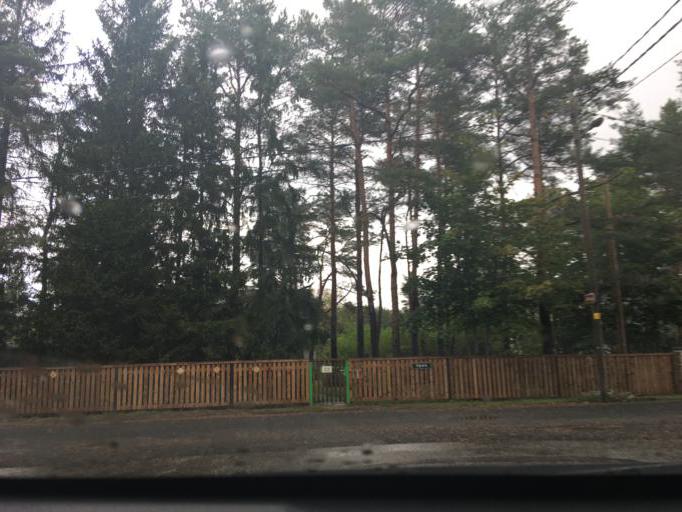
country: EE
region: Harju
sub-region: Saue vald
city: Laagri
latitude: 59.3717
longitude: 24.6741
